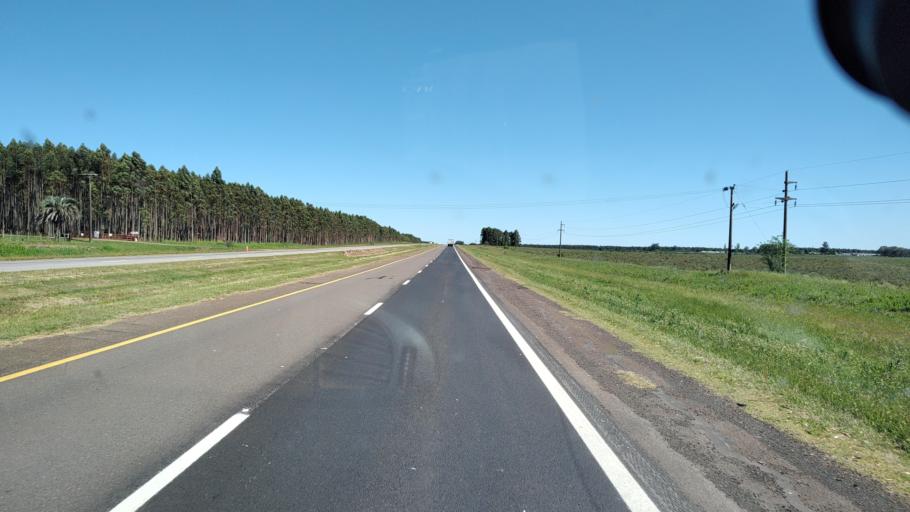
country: AR
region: Entre Rios
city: Colon
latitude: -32.1210
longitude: -58.2419
